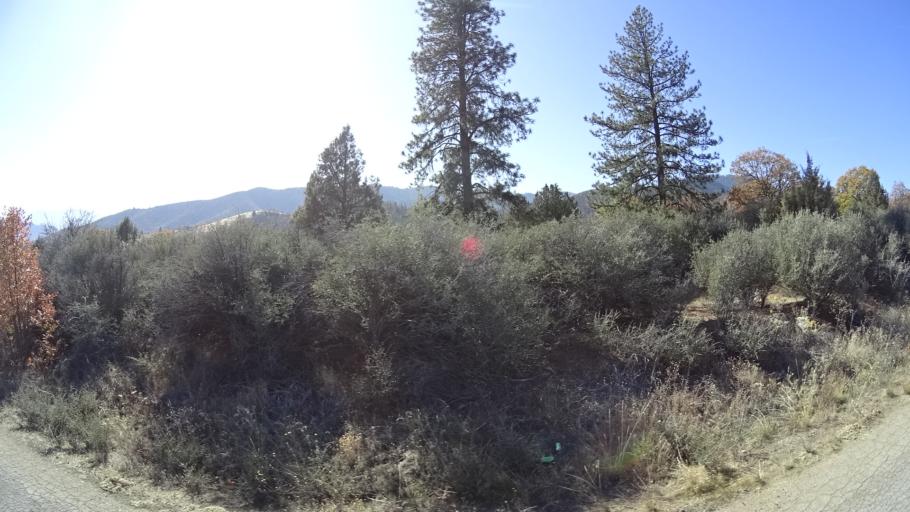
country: US
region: California
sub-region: Siskiyou County
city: Yreka
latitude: 41.7738
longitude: -122.6374
